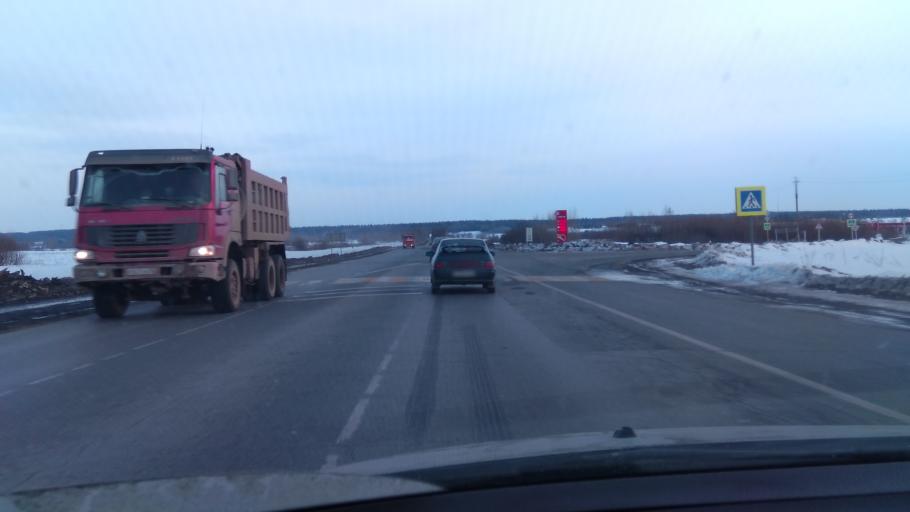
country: RU
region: Perm
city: Kukushtan
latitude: 57.5054
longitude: 56.6500
